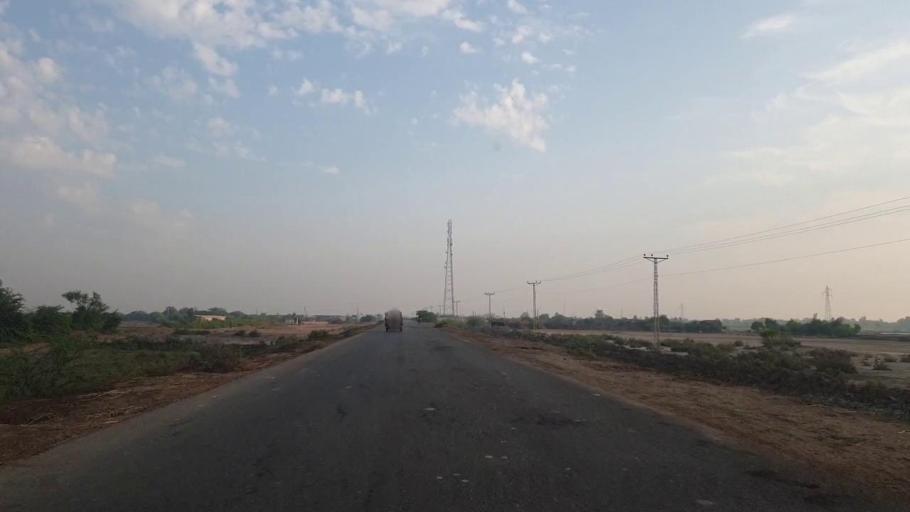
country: PK
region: Sindh
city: Badin
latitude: 24.6961
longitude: 68.9200
